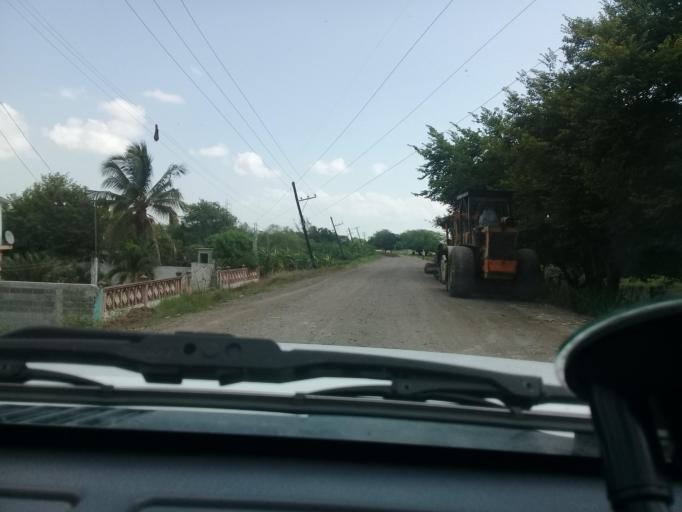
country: MX
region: Veracruz
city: Moralillo
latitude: 22.1783
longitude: -97.9481
